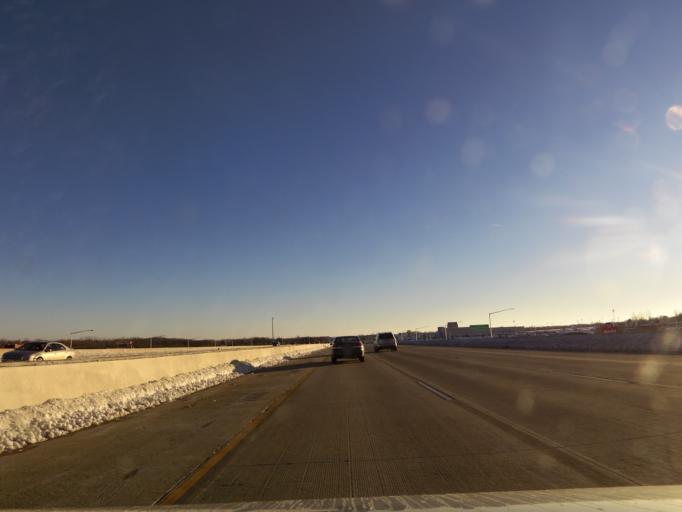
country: US
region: Wisconsin
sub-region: Kenosha County
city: Pleasant Prairie
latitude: 42.5701
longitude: -87.9529
